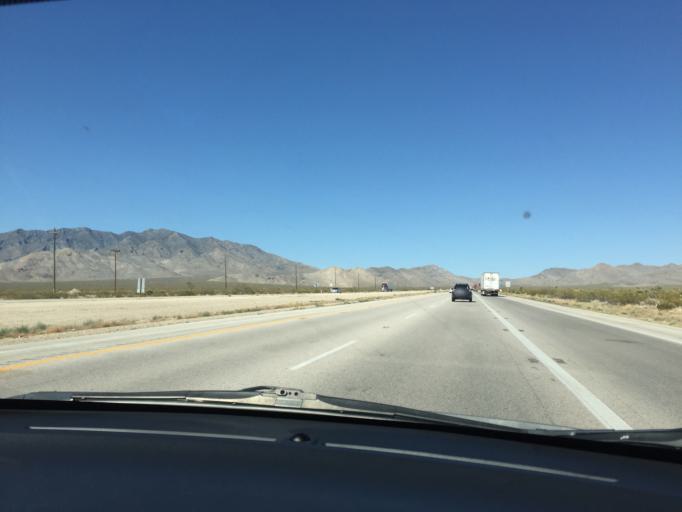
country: US
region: Nevada
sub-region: Clark County
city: Sandy Valley
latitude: 35.4502
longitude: -115.6563
